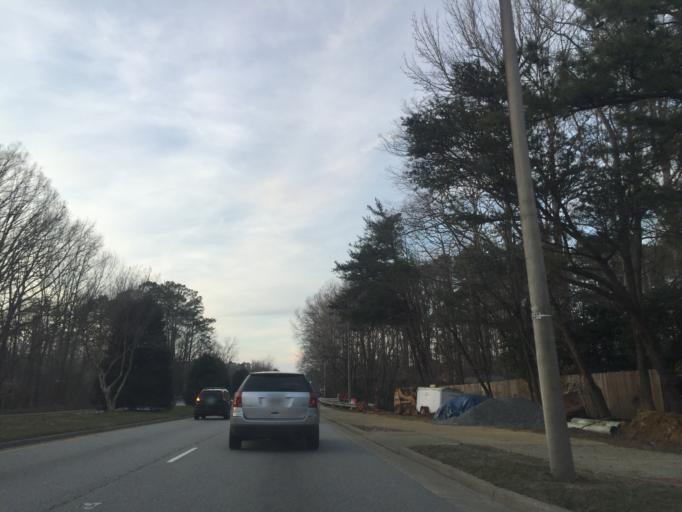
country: US
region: Virginia
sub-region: York County
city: Yorktown
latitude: 37.1015
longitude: -76.5103
